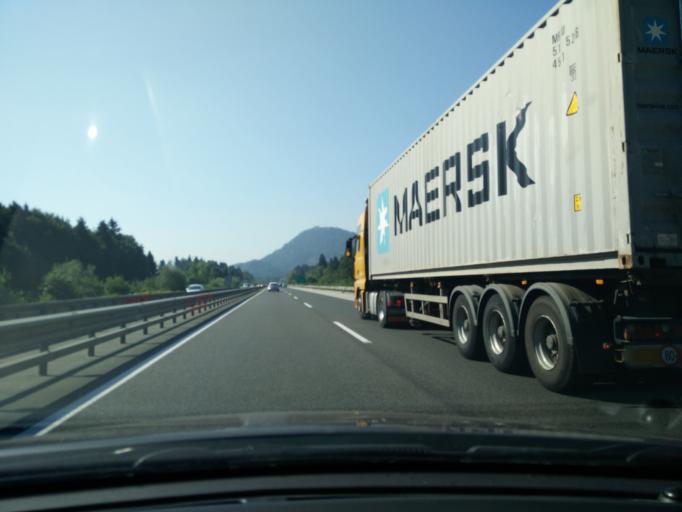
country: SI
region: Vodice
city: Vodice
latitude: 46.1591
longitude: 14.4814
